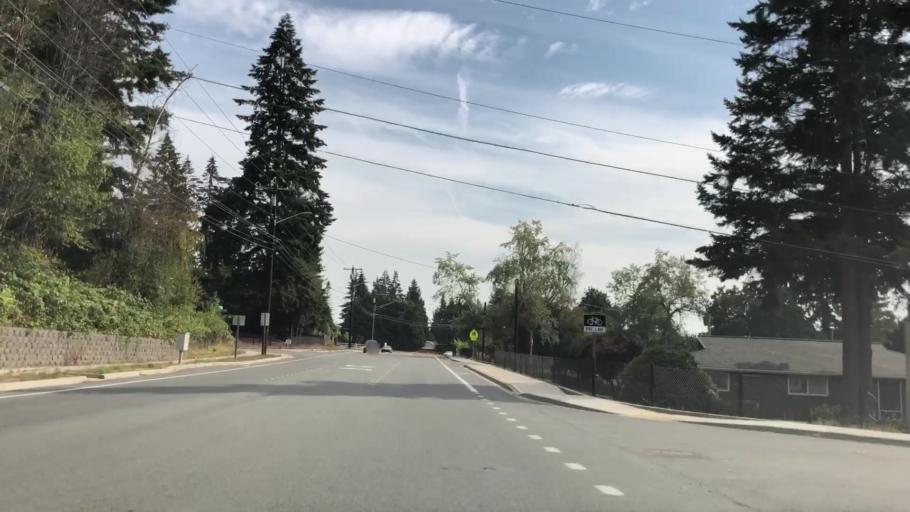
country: US
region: Washington
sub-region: Snohomish County
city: Martha Lake
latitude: 47.8367
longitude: -122.2370
